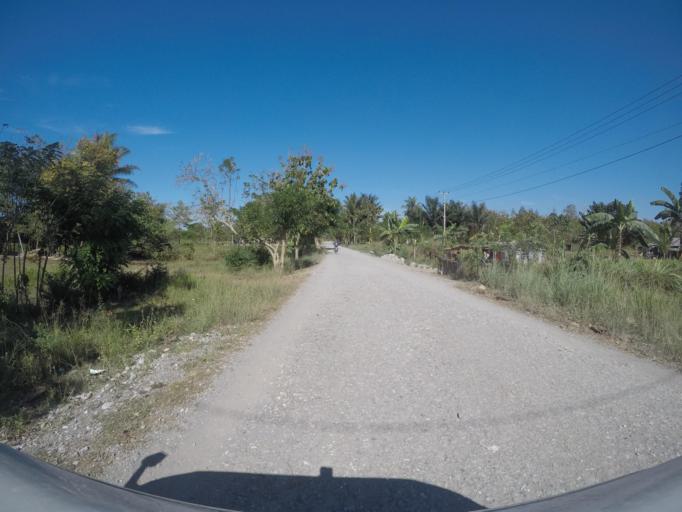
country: TL
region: Viqueque
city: Viqueque
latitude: -8.9341
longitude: 126.1272
